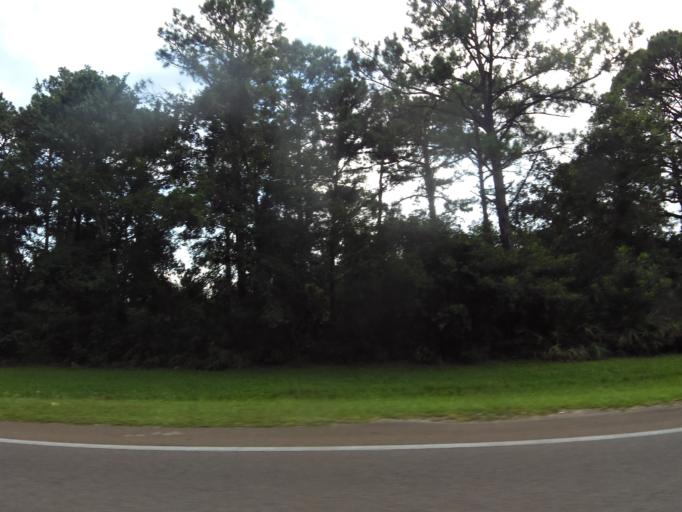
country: US
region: Florida
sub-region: Nassau County
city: Fernandina Beach
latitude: 30.6218
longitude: -81.4679
